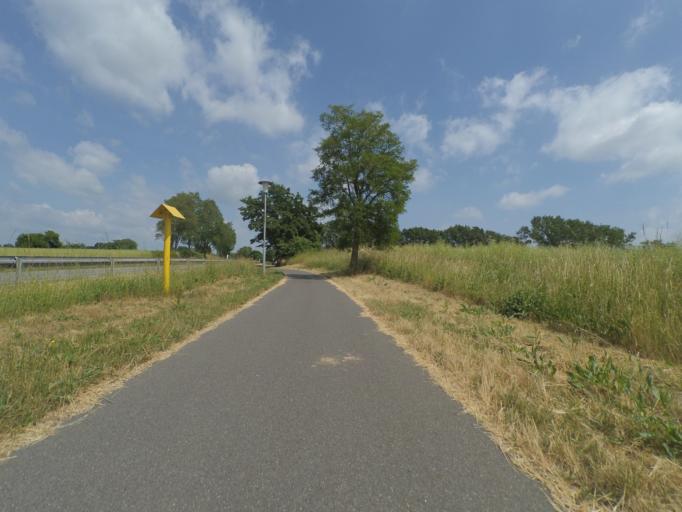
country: DE
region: Mecklenburg-Vorpommern
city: Lubz
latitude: 53.4608
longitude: 12.0137
